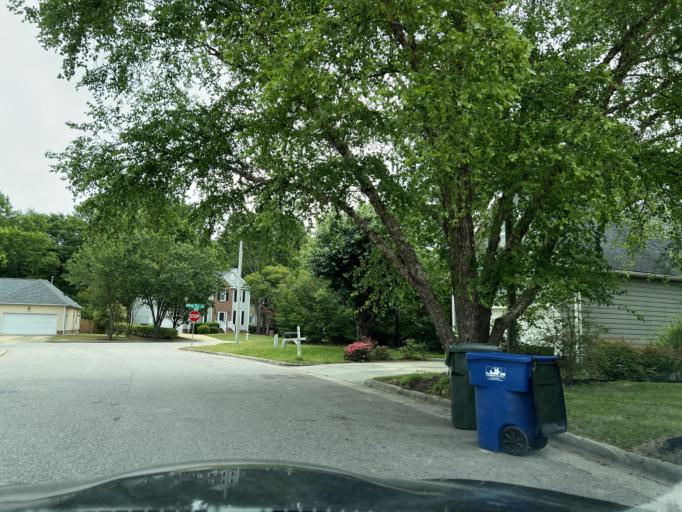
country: US
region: North Carolina
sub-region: Wake County
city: Knightdale
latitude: 35.8668
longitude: -78.5517
